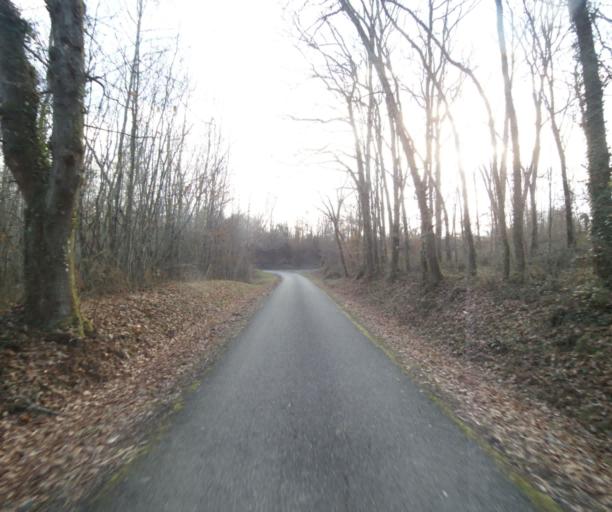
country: FR
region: Midi-Pyrenees
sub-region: Departement du Tarn-et-Garonne
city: Moissac
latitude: 44.1236
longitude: 1.0441
